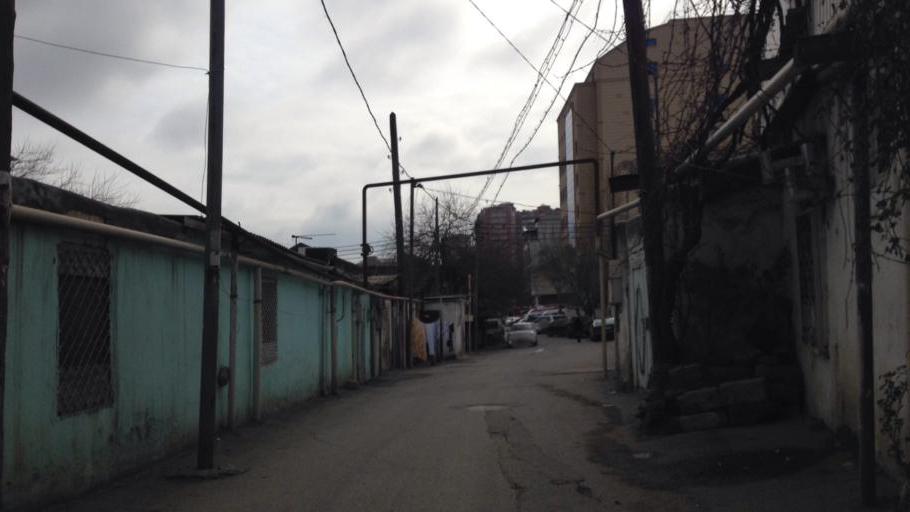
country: AZ
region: Baki
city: Bilajari
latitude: 40.3992
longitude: 49.8283
